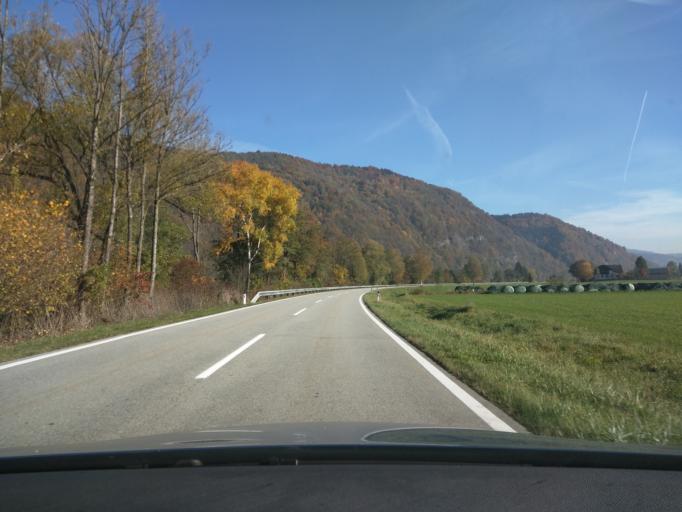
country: DE
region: Bavaria
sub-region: Lower Bavaria
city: Obernzell
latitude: 48.5674
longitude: 13.5947
